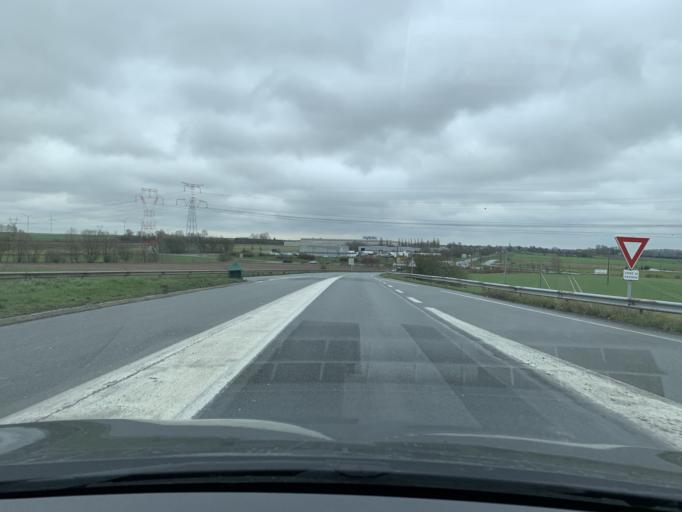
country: FR
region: Nord-Pas-de-Calais
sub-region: Departement du Nord
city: Hordain
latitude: 50.2526
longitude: 3.3219
